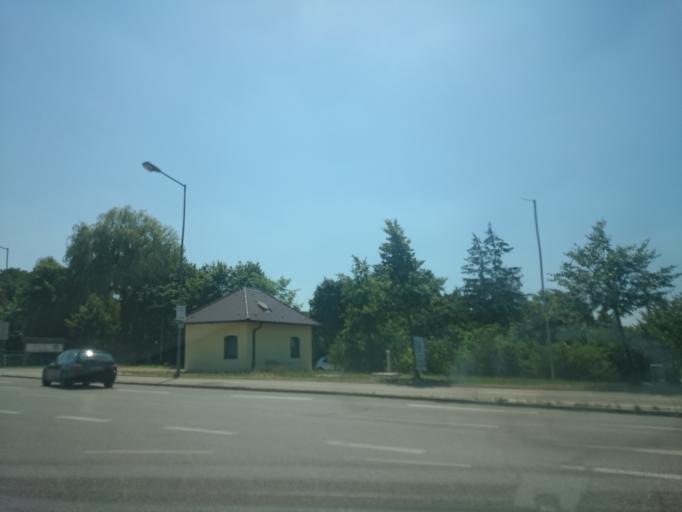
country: DE
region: Bavaria
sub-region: Swabia
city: Augsburg
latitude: 48.3699
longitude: 10.8784
